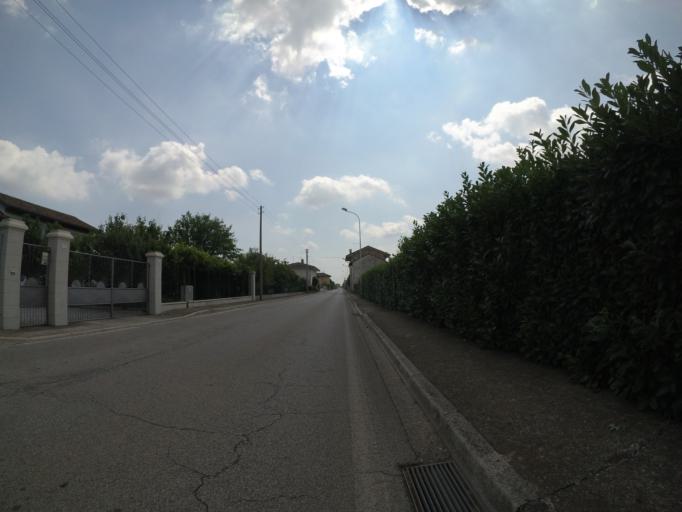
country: IT
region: Friuli Venezia Giulia
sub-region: Provincia di Udine
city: Basiliano
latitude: 46.0105
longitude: 13.0706
